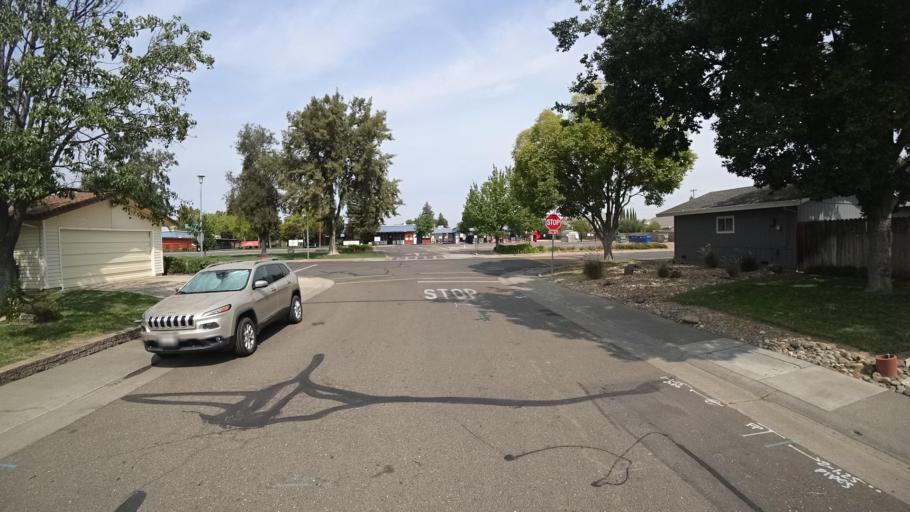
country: US
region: California
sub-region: Sacramento County
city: Elk Grove
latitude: 38.4192
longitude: -121.3769
